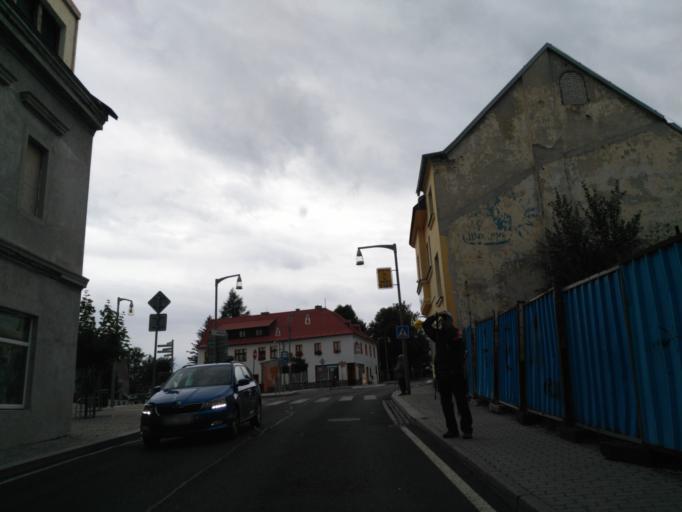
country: CZ
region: Karlovarsky
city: Abertamy
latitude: 50.3686
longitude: 12.8180
